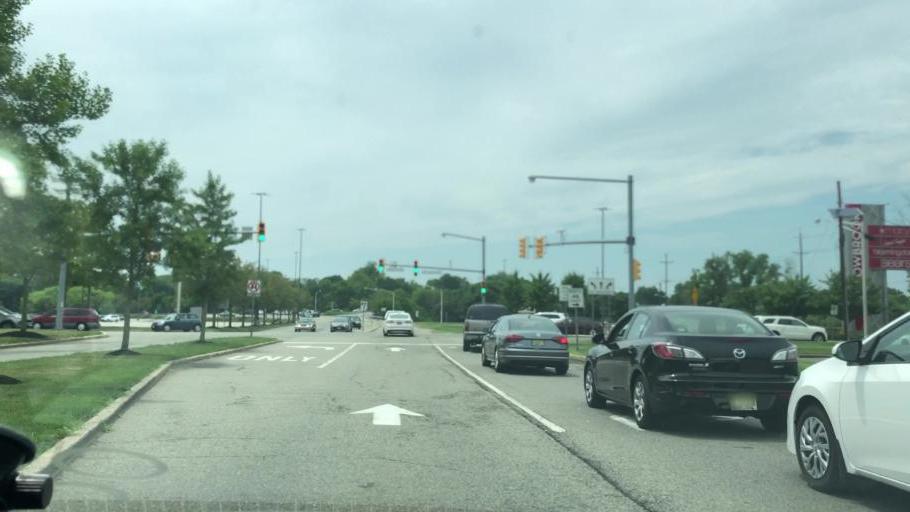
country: US
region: New Jersey
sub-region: Passaic County
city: Singac
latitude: 40.8924
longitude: -74.2594
